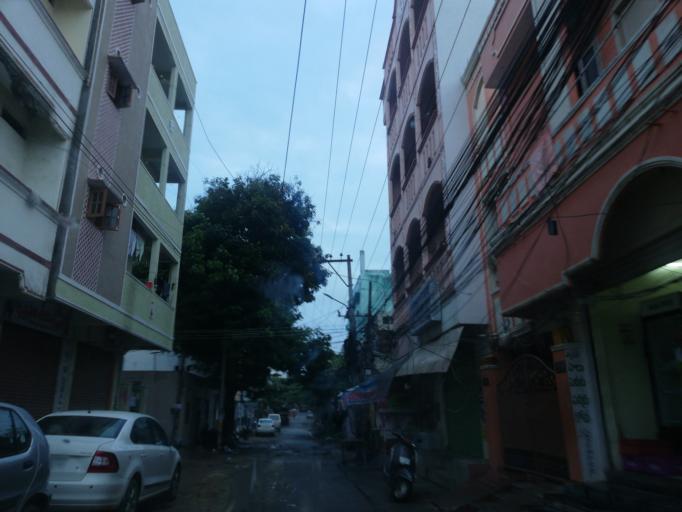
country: IN
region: Telangana
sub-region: Rangareddi
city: Kukatpalli
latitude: 17.4890
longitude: 78.3970
